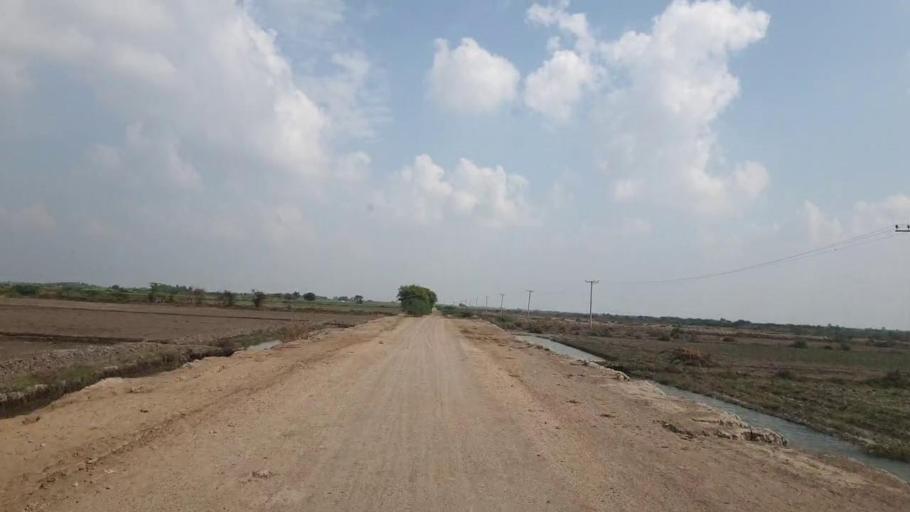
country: PK
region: Sindh
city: Badin
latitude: 24.5328
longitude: 68.6204
